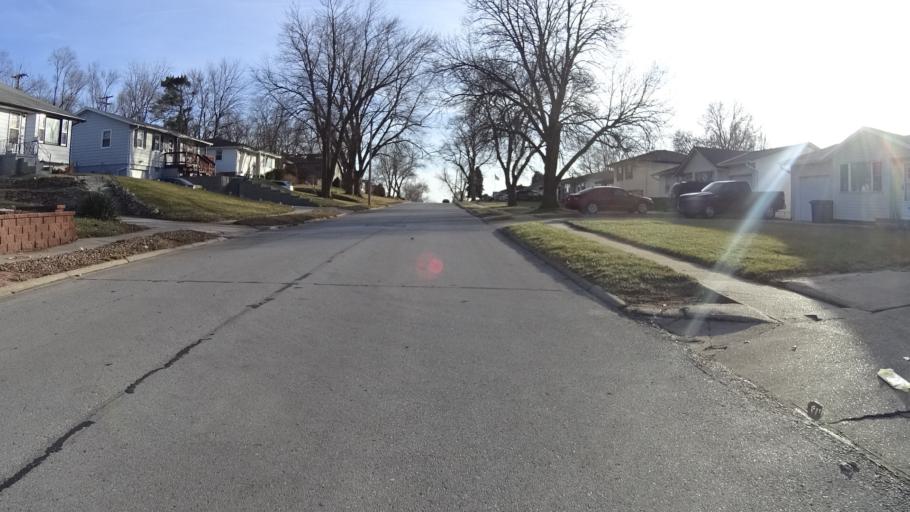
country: US
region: Nebraska
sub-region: Sarpy County
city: La Vista
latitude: 41.1899
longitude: -95.9969
